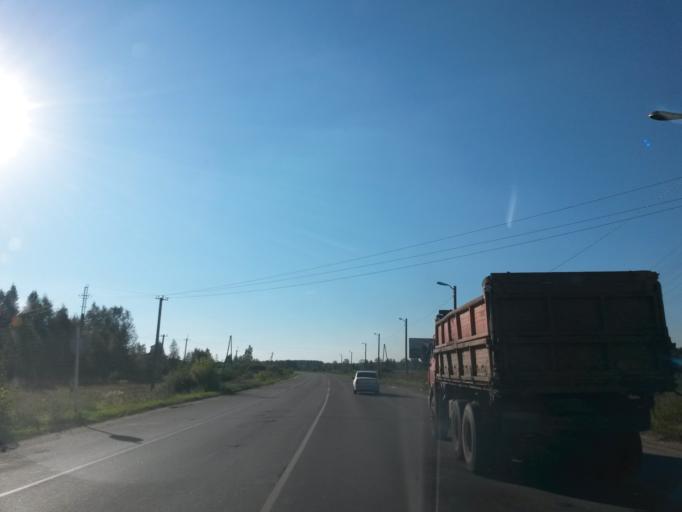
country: RU
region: Ivanovo
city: Novo-Talitsy
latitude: 57.0100
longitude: 40.8374
